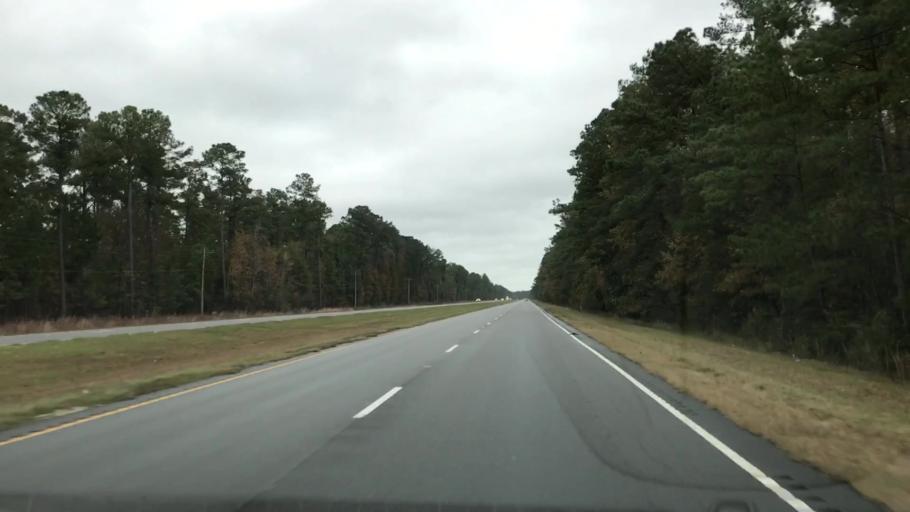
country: US
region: South Carolina
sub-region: Georgetown County
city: Georgetown
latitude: 33.2570
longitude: -79.3696
